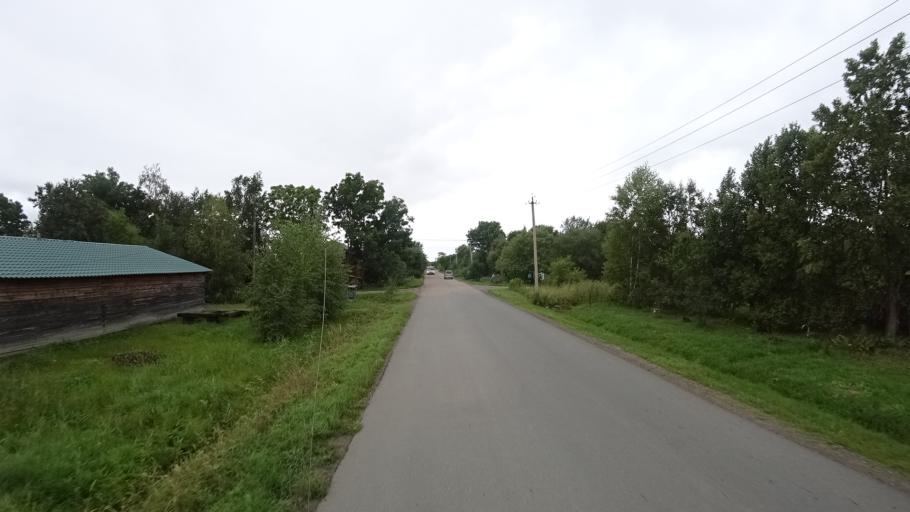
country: RU
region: Primorskiy
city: Chernigovka
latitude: 44.3489
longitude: 132.5659
